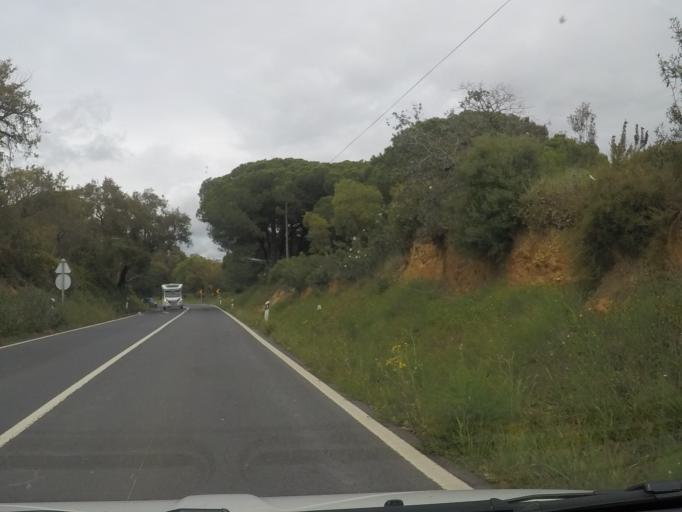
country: PT
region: Setubal
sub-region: Sines
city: Porto Covo
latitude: 37.8727
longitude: -8.7431
